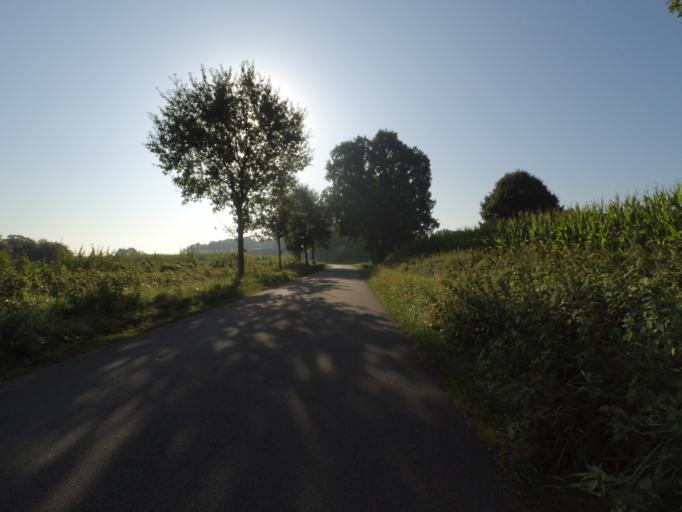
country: DE
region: Lower Saxony
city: Suddendorf
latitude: 52.2889
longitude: 7.1945
